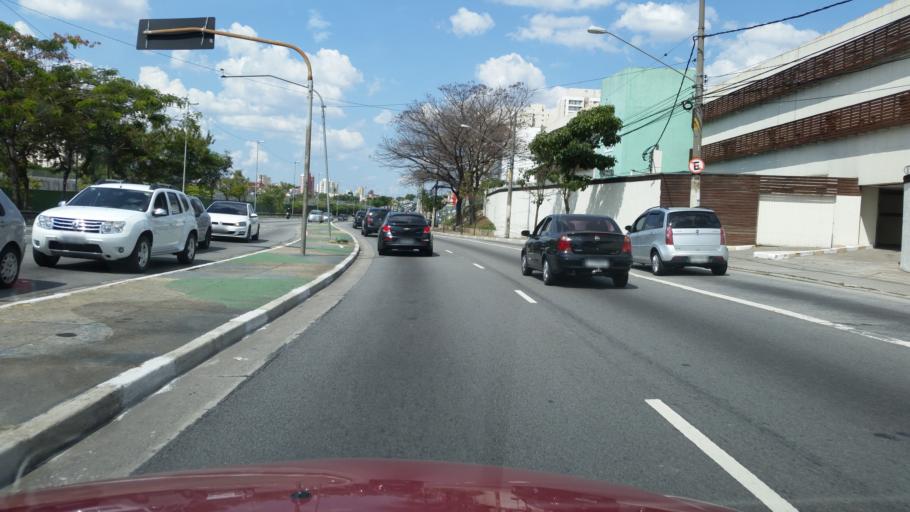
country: BR
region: Sao Paulo
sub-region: Guarulhos
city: Guarulhos
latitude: -23.5331
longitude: -46.5381
